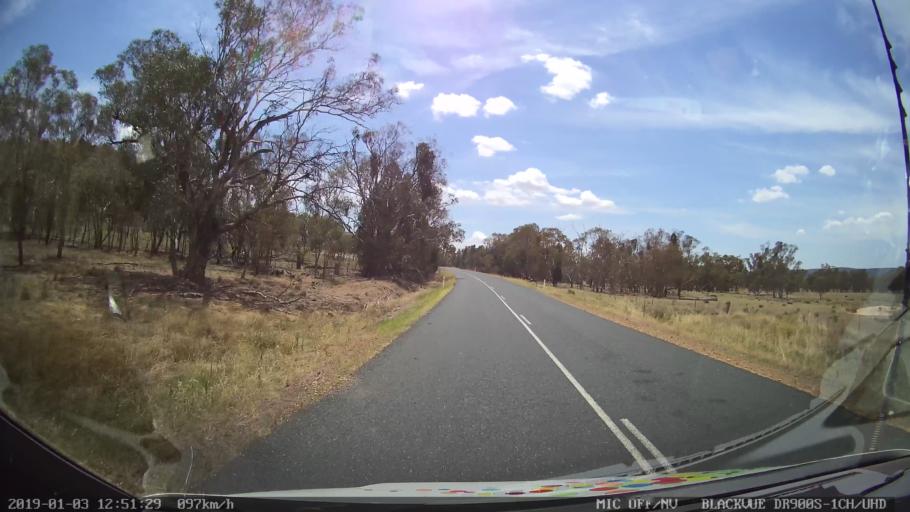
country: AU
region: New South Wales
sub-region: Weddin
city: Grenfell
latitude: -33.6794
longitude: 148.2813
